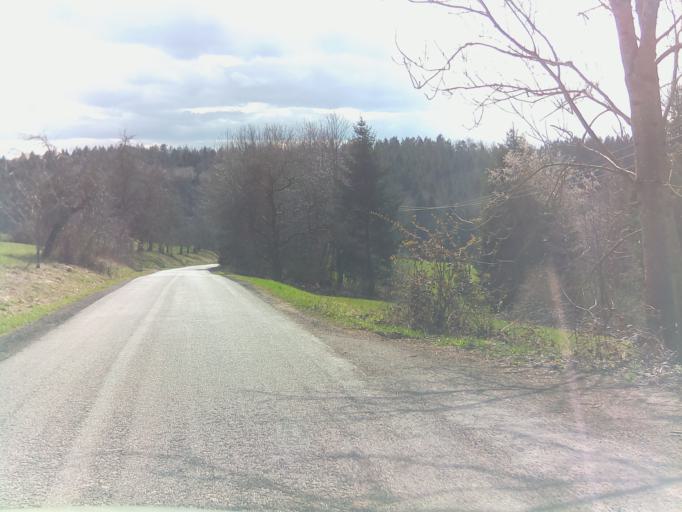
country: DE
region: Baden-Wuerttemberg
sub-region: Regierungsbezirk Stuttgart
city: Welzheim
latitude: 48.8672
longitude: 9.5947
